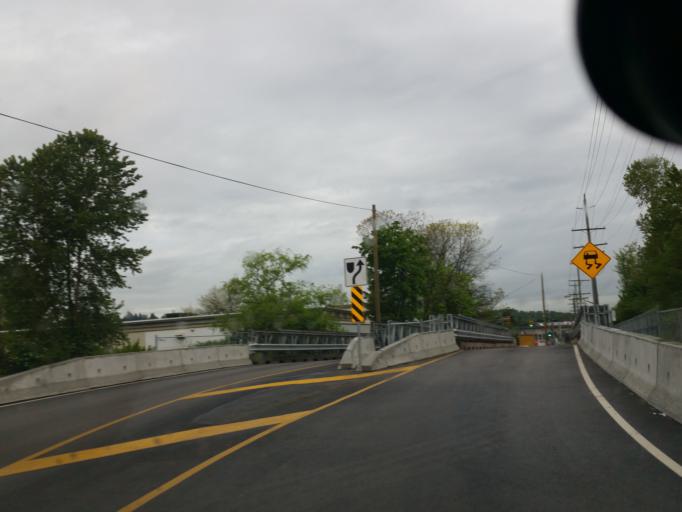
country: CA
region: British Columbia
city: New Westminster
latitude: 49.2290
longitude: -122.8767
